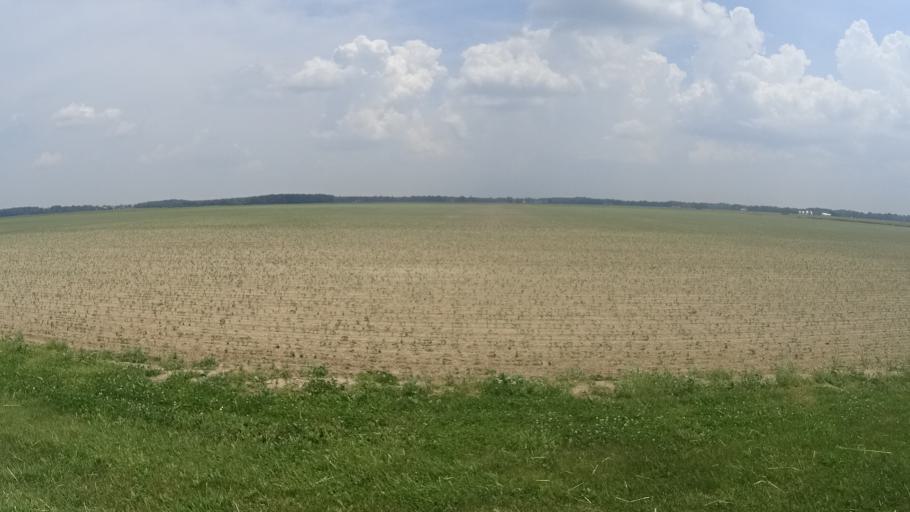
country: US
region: Ohio
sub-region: Huron County
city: Monroeville
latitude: 41.2971
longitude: -82.6923
